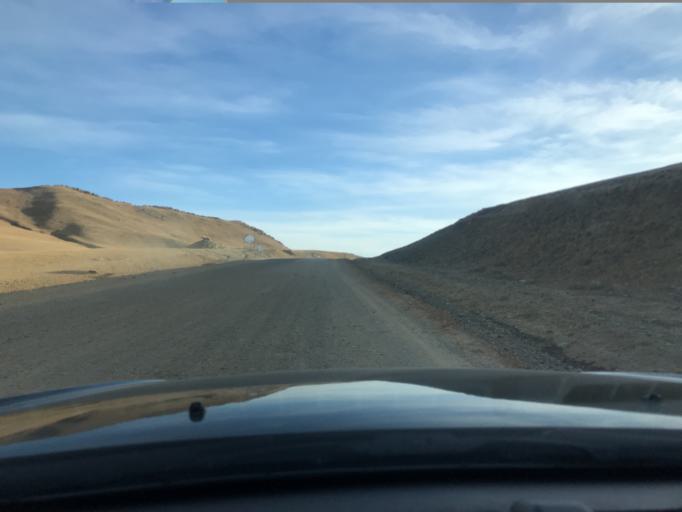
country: MN
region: Central Aimak
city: Dzuunmod
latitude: 47.8126
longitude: 107.3273
